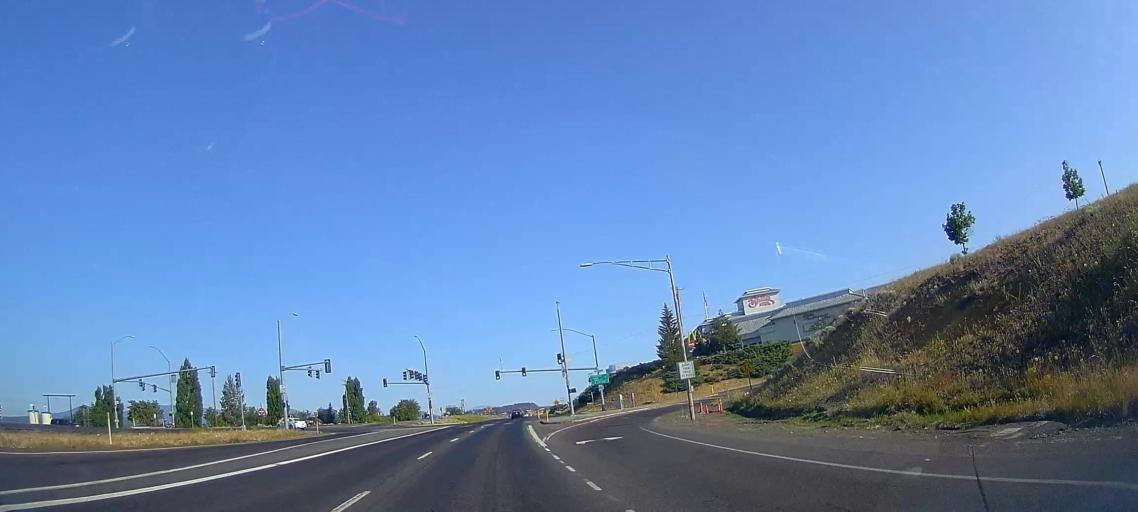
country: US
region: Oregon
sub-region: Klamath County
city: Klamath Falls
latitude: 42.2481
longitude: -121.7905
